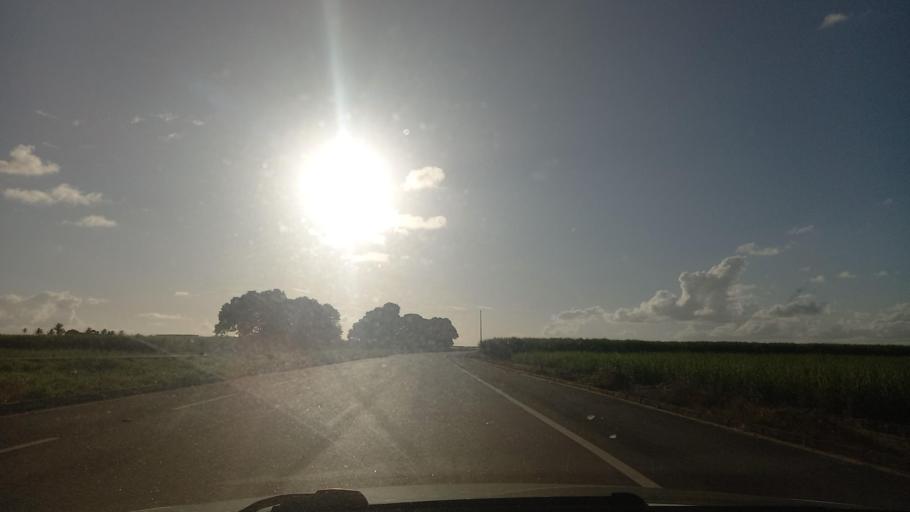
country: BR
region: Alagoas
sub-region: Campo Alegre
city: Campo Alegre
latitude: -9.8061
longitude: -36.2623
